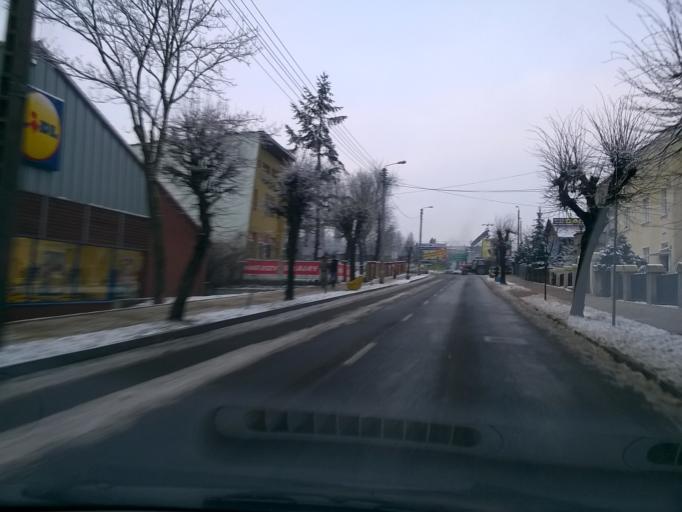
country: PL
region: Kujawsko-Pomorskie
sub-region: Powiat nakielski
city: Naklo nad Notecia
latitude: 53.1407
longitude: 17.6039
